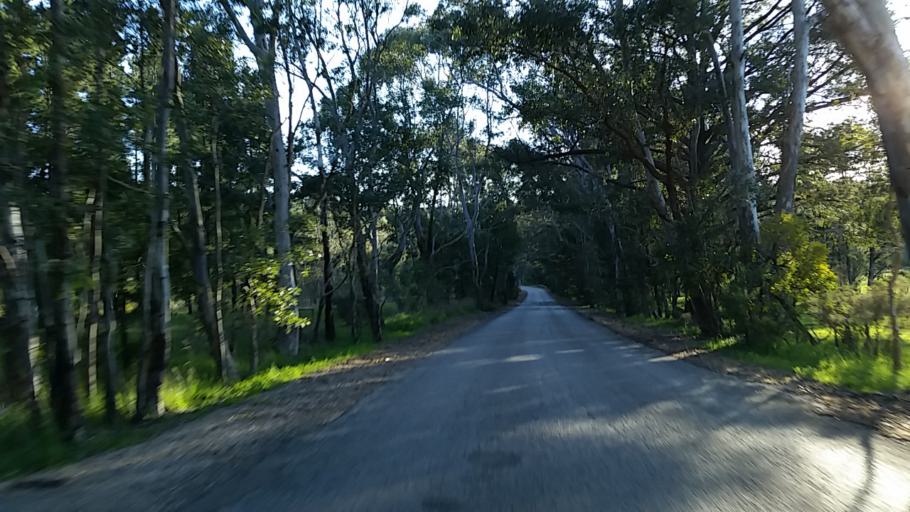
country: AU
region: South Australia
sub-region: Mount Barker
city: Meadows
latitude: -35.2342
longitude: 138.7151
